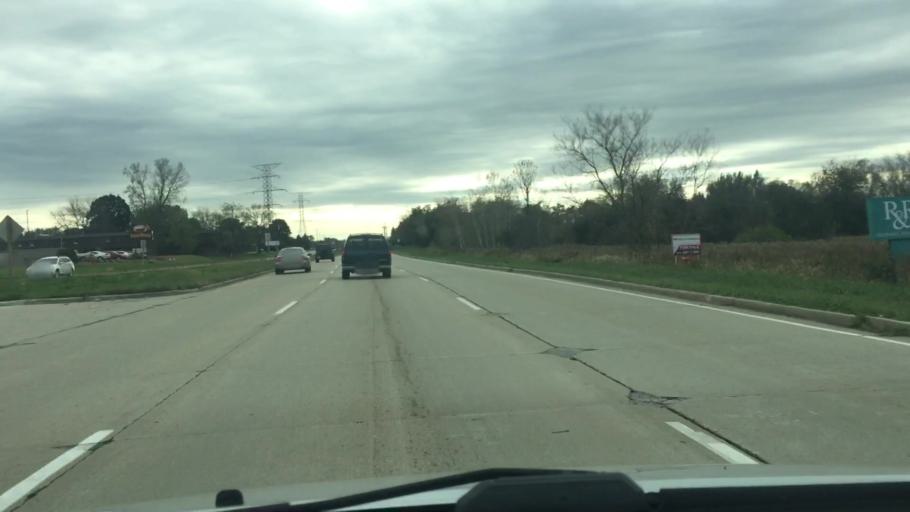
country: US
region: Wisconsin
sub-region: Waukesha County
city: Waukesha
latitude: 42.9953
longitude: -88.2023
